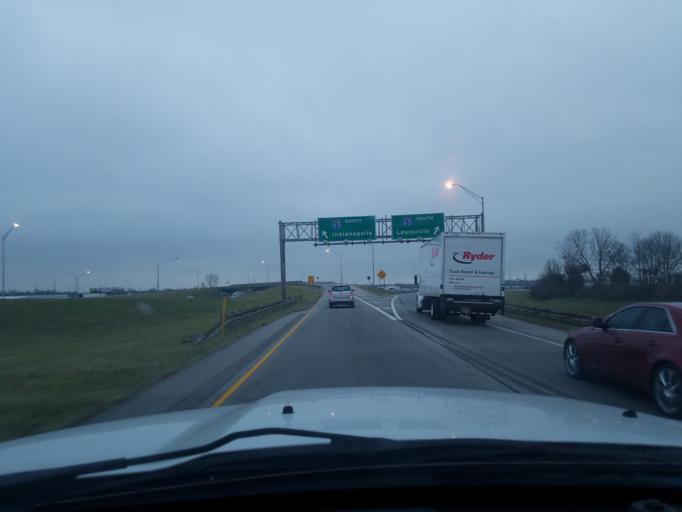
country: US
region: Indiana
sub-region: Clark County
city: Clarksville
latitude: 38.3448
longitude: -85.7570
